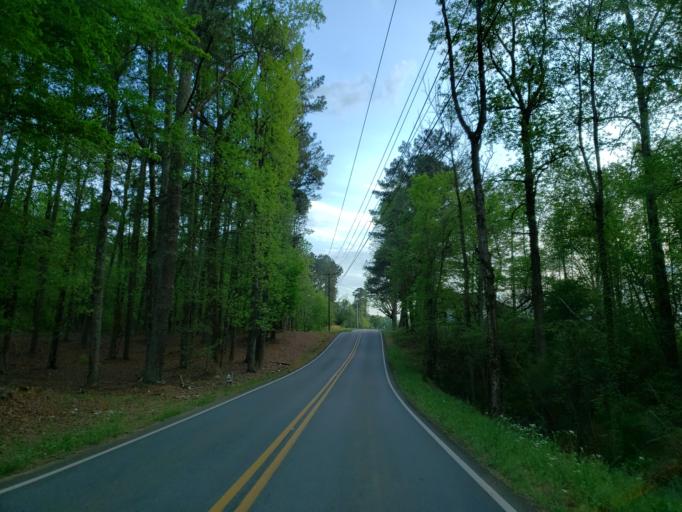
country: US
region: Georgia
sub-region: Cherokee County
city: Canton
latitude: 34.2948
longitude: -84.4505
